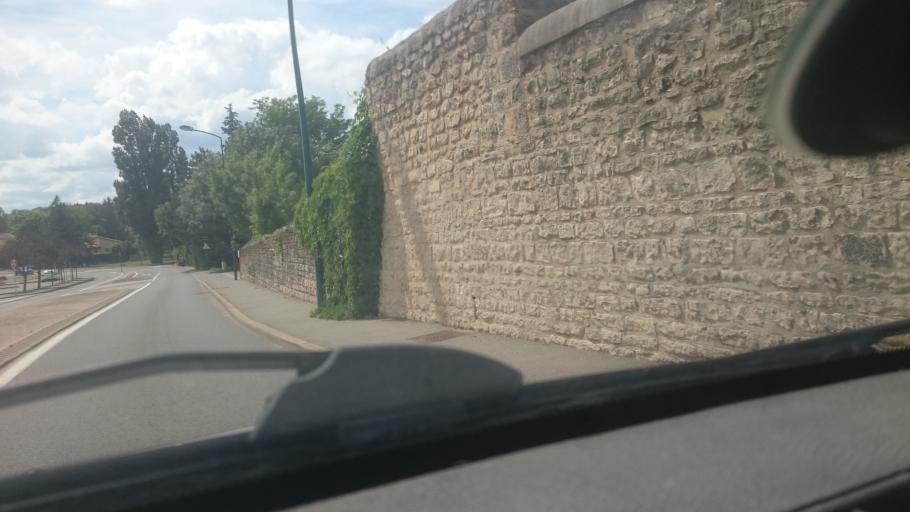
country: FR
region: Rhone-Alpes
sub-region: Departement du Rhone
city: Morance
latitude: 45.8744
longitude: 4.7074
